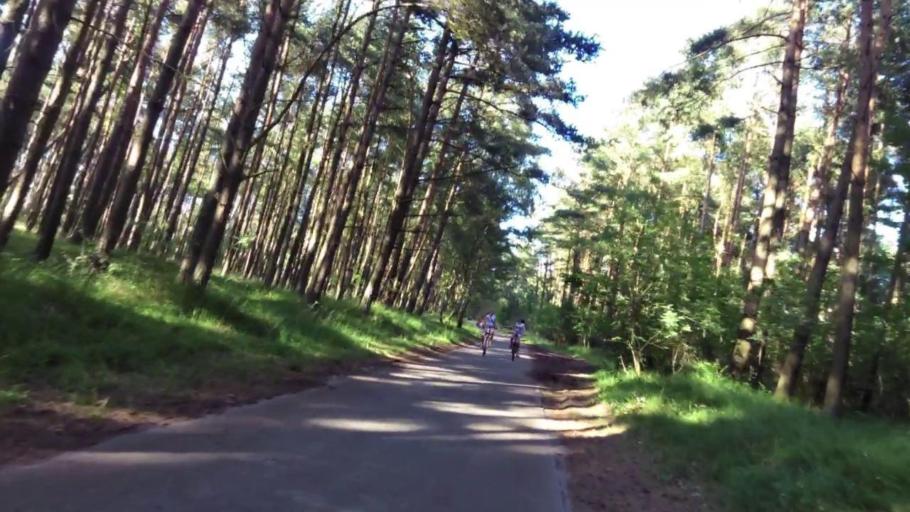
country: PL
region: West Pomeranian Voivodeship
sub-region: Powiat slawienski
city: Darlowo
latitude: 54.3691
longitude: 16.2967
